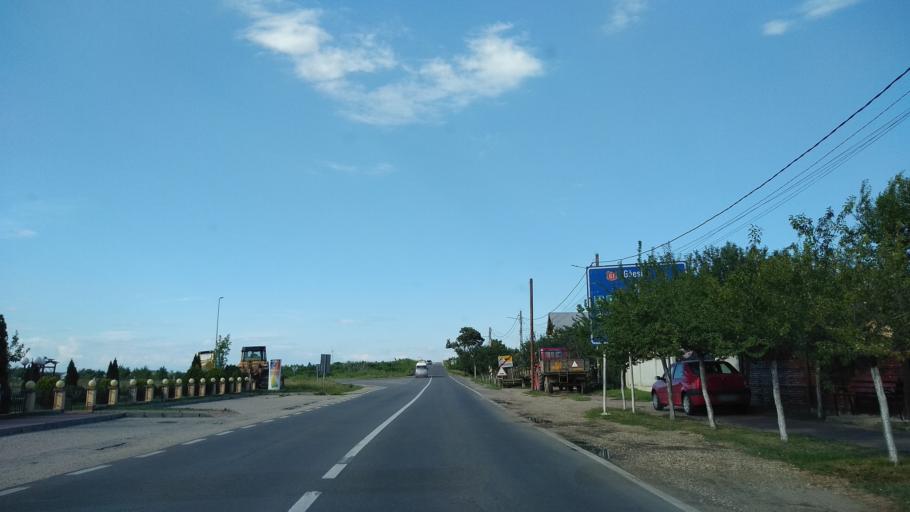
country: RO
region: Dambovita
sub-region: Comuna Petresti
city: Petresti
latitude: 44.6542
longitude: 25.3364
